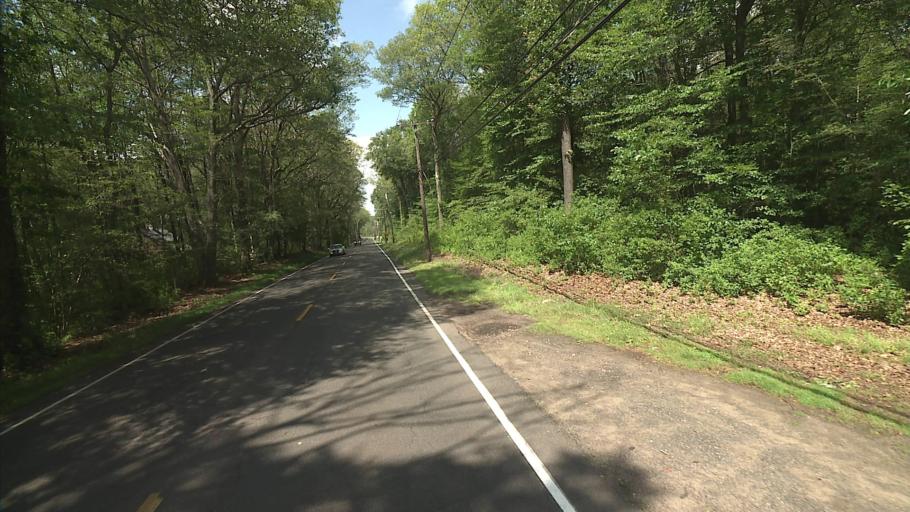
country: US
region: Connecticut
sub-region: Middlesex County
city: Higganum
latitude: 41.4251
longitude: -72.5617
